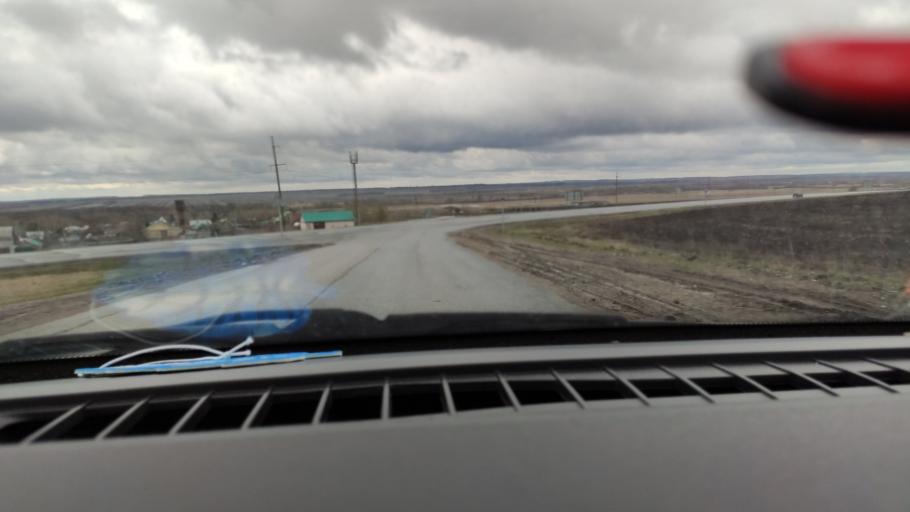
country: RU
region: Tatarstan
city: Nurlat
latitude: 54.3966
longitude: 50.7802
